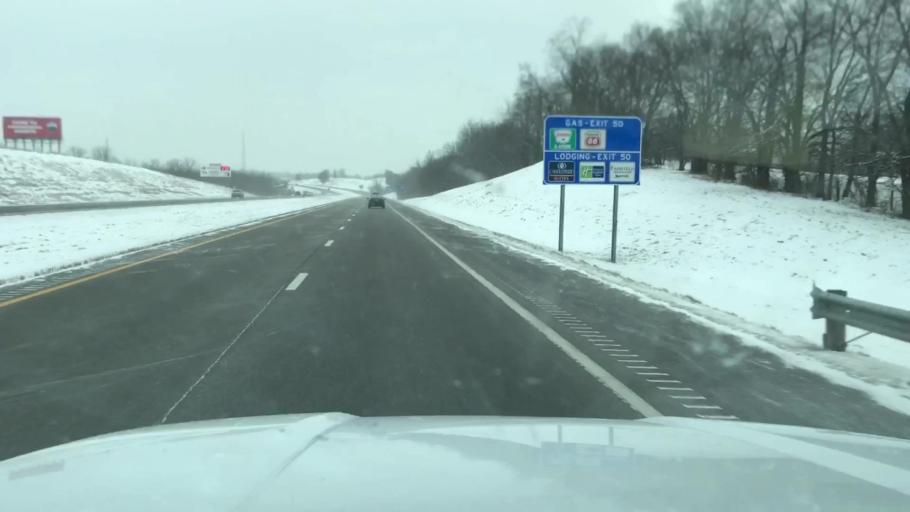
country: US
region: Missouri
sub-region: Andrew County
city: Country Club Village
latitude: 39.8277
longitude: -94.8055
